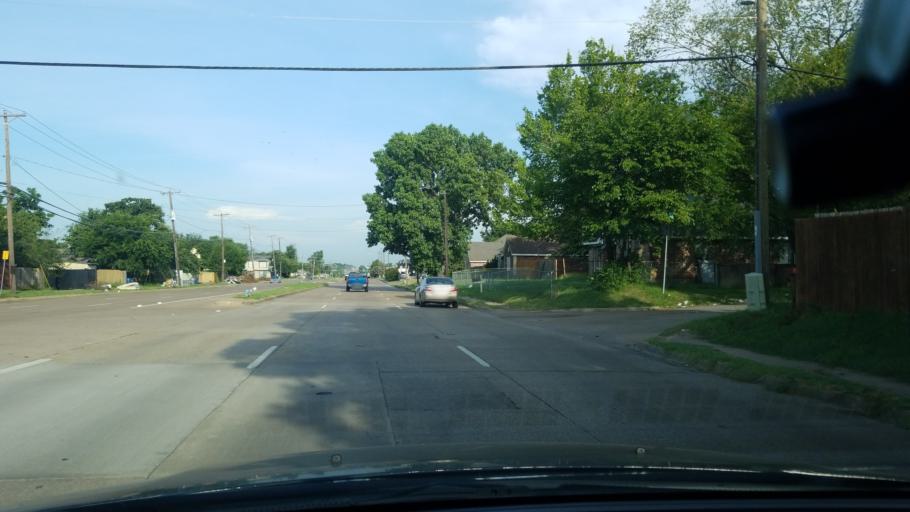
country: US
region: Texas
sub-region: Dallas County
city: Balch Springs
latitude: 32.7487
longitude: -96.6502
